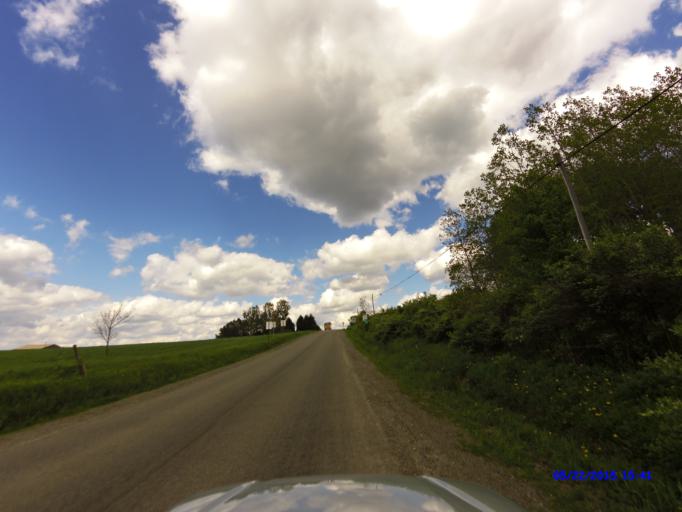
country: US
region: New York
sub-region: Cattaraugus County
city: Franklinville
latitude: 42.3133
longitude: -78.5837
